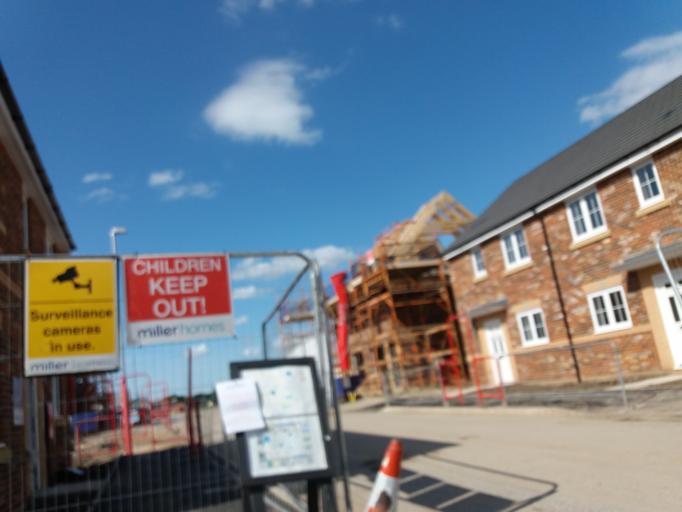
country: GB
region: England
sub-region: Lancashire
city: Coppull
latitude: 53.6273
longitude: -2.6632
